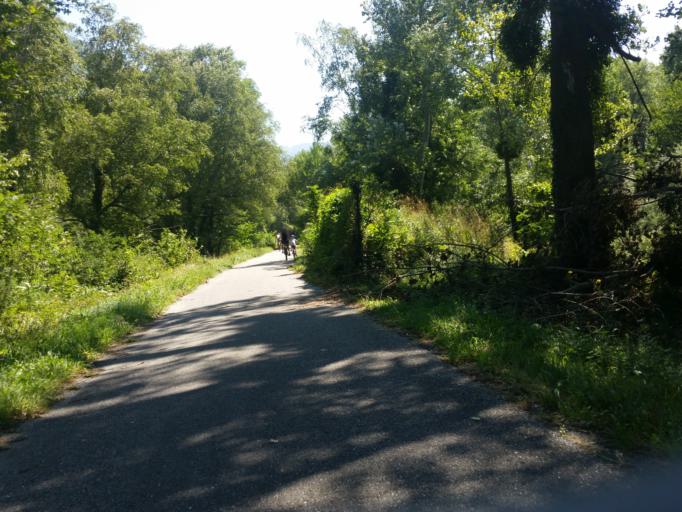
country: CH
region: Valais
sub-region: Saint-Maurice District
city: Vernayaz
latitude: 46.1418
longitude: 7.0456
